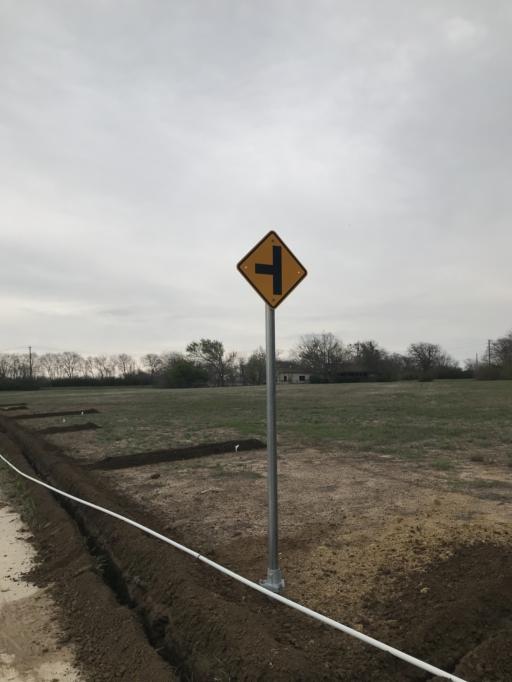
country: US
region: Texas
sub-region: Denton County
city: Denton
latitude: 33.2446
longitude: -97.1457
